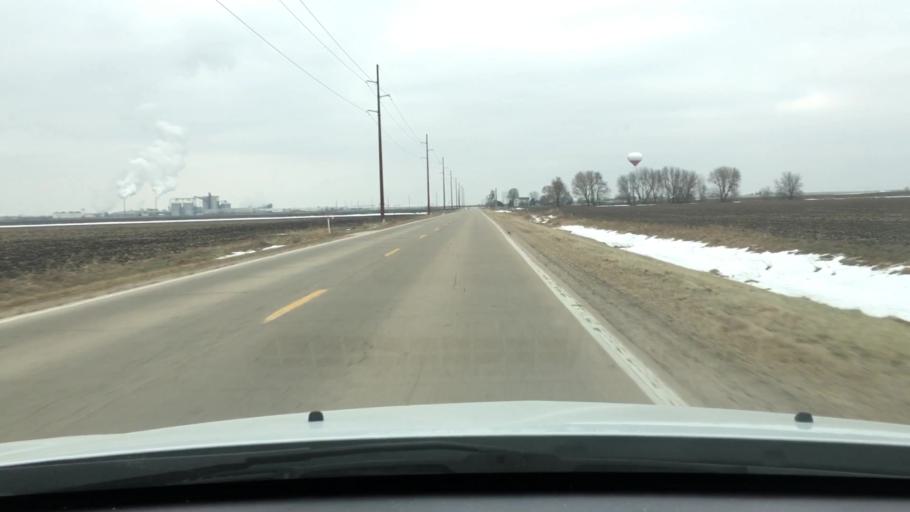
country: US
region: Illinois
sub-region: Ogle County
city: Rochelle
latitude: 41.8733
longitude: -89.0250
